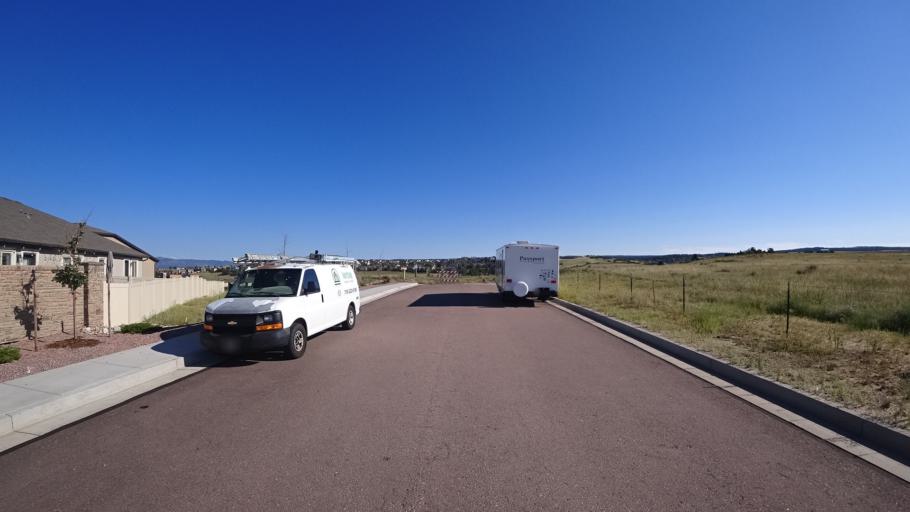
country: US
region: Colorado
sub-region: El Paso County
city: Gleneagle
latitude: 38.9964
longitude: -104.7888
